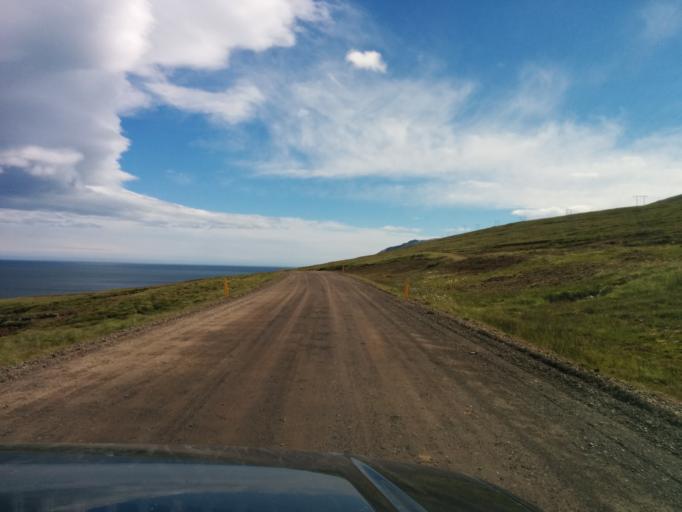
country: IS
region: East
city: Egilsstadir
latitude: 65.7491
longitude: -14.6442
